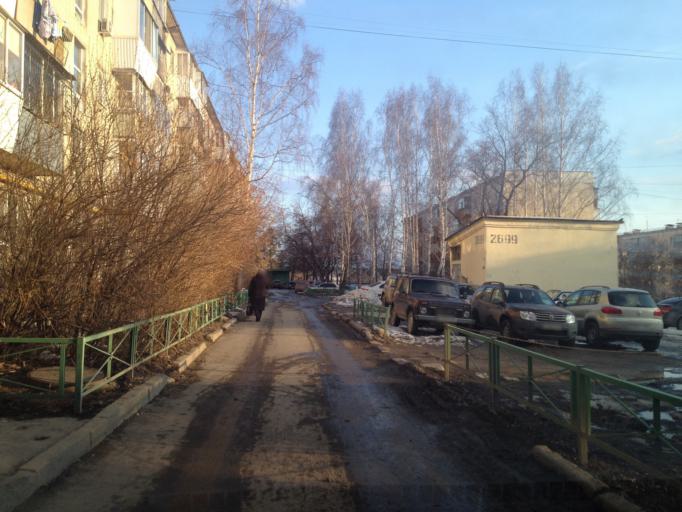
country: RU
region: Sverdlovsk
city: Sovkhoznyy
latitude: 56.7641
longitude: 60.6036
